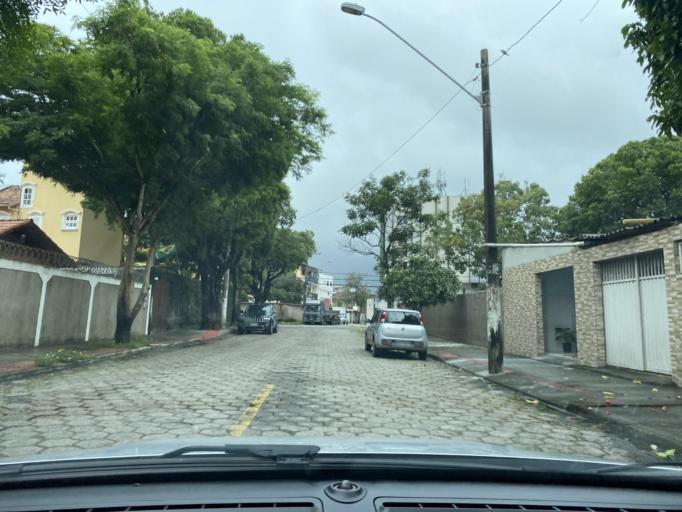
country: BR
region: Espirito Santo
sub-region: Vila Velha
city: Vila Velha
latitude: -20.2599
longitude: -40.2935
